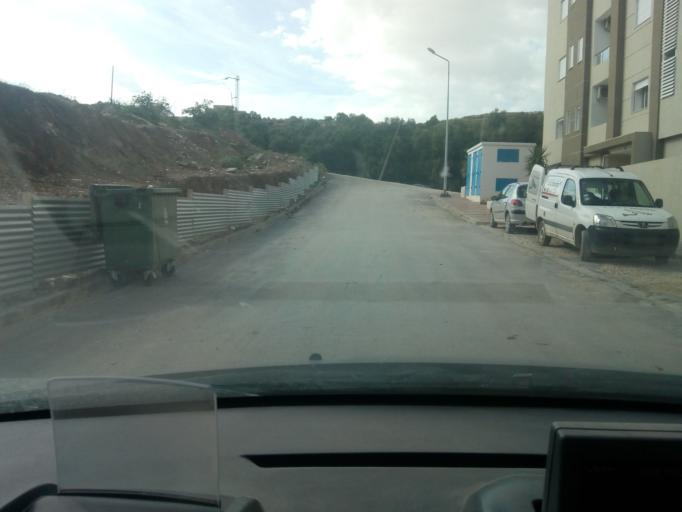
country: TN
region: Ariana
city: Ariana
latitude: 36.8764
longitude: 10.1778
